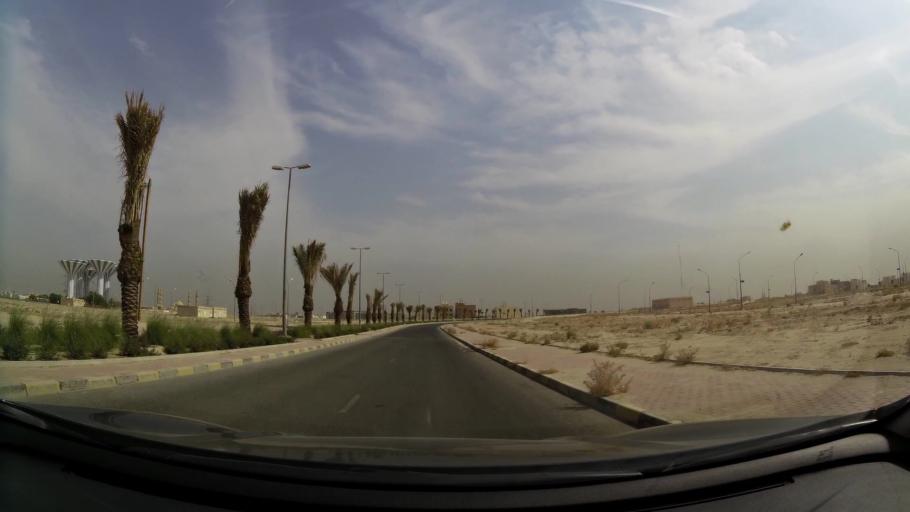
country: KW
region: Al Farwaniyah
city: Janub as Surrah
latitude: 29.2996
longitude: 47.9929
